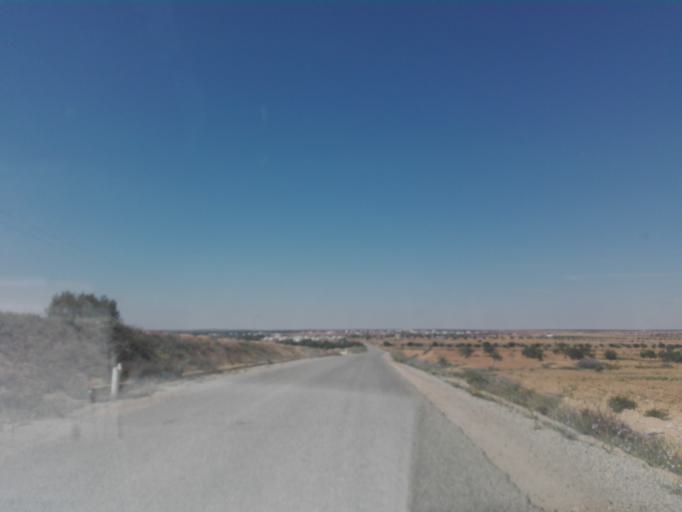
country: TN
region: Safaqis
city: Bi'r `Ali Bin Khalifah
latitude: 34.6733
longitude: 10.3782
